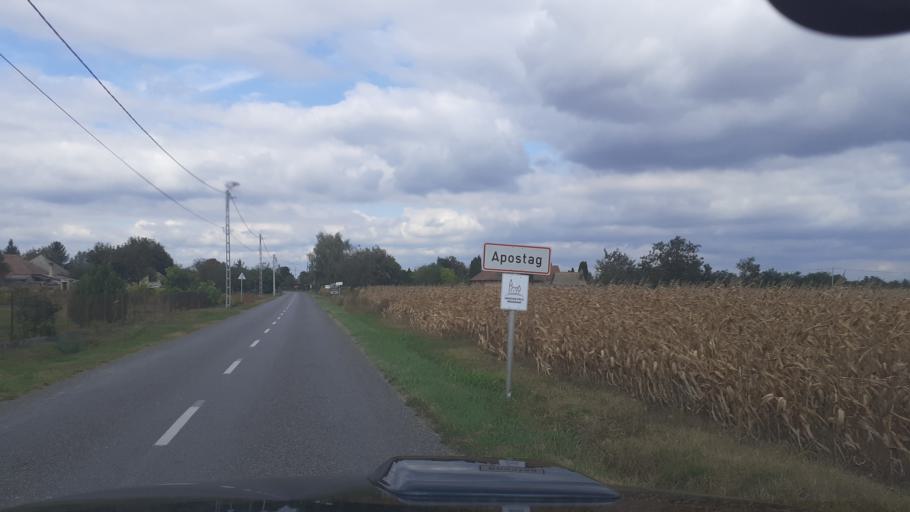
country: HU
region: Bacs-Kiskun
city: Apostag
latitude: 46.8705
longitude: 18.9559
